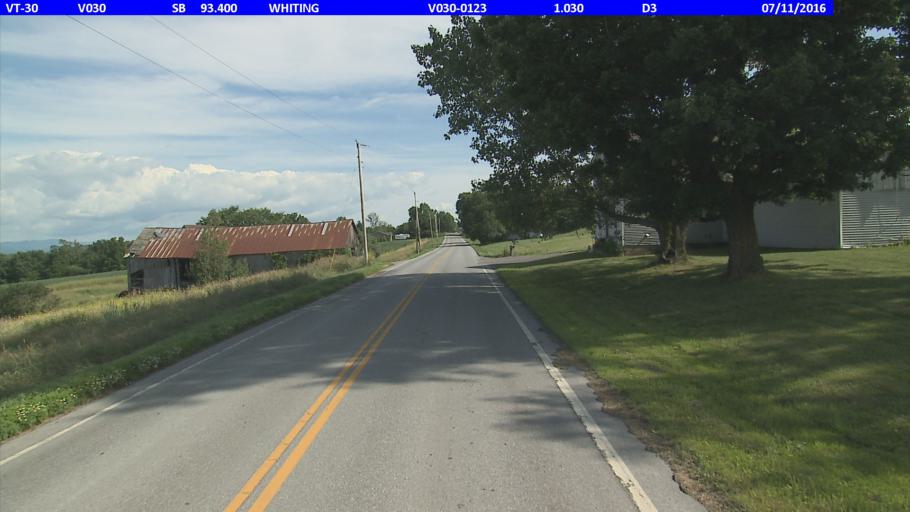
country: US
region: Vermont
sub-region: Rutland County
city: Brandon
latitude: 43.8526
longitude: -73.2001
